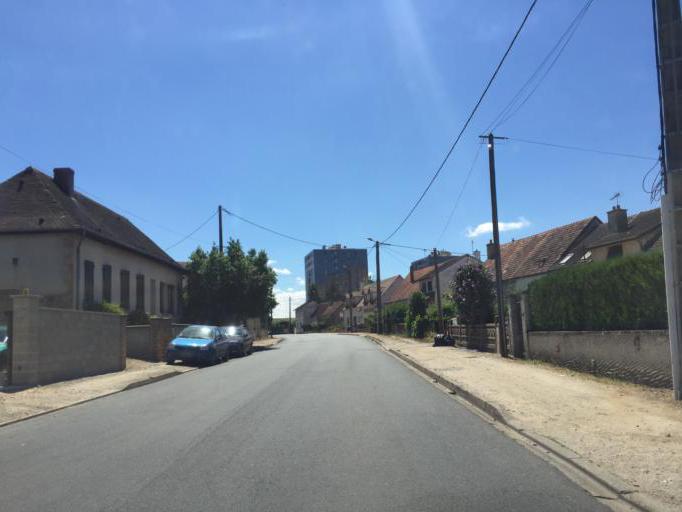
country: FR
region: Auvergne
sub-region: Departement de l'Allier
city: Moulins
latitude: 46.5830
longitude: 3.3330
